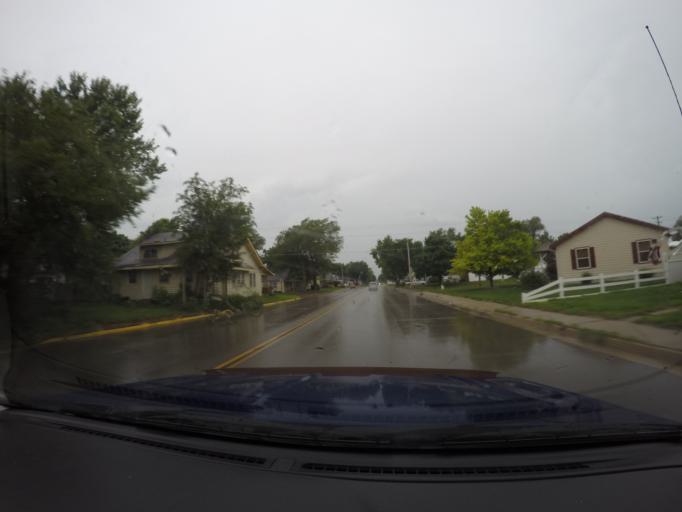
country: US
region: Kansas
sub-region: Cloud County
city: Concordia
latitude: 39.5715
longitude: -97.6478
